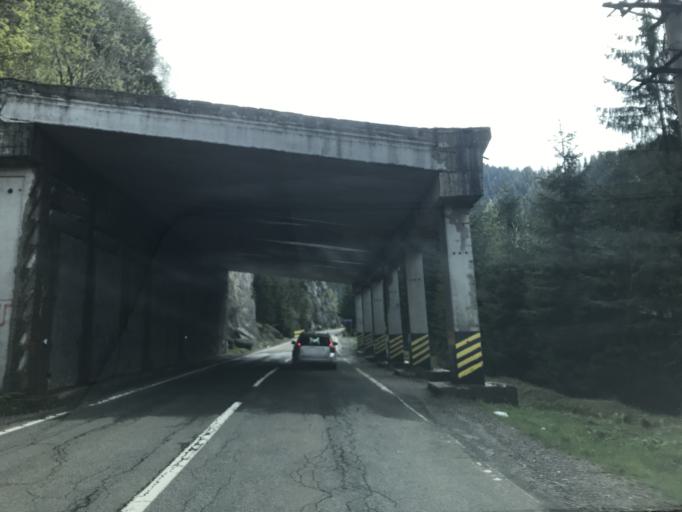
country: RO
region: Sibiu
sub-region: Comuna Cartisoara
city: Cartisoara
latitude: 45.6439
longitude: 24.6055
